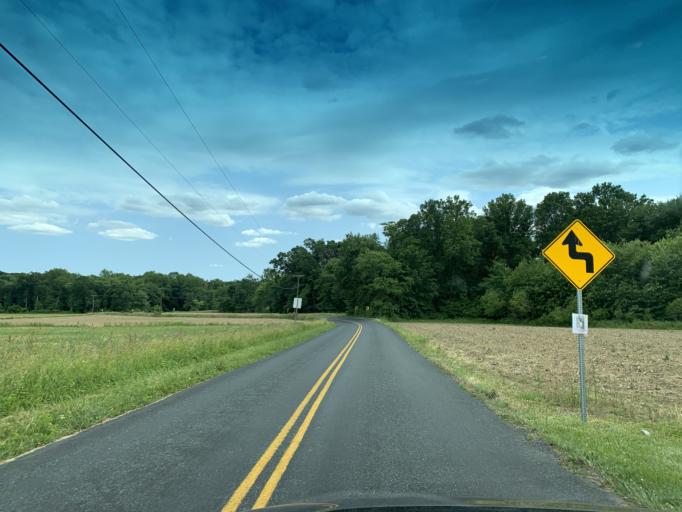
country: US
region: Maryland
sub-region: Harford County
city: Jarrettsville
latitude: 39.6162
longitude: -76.4991
